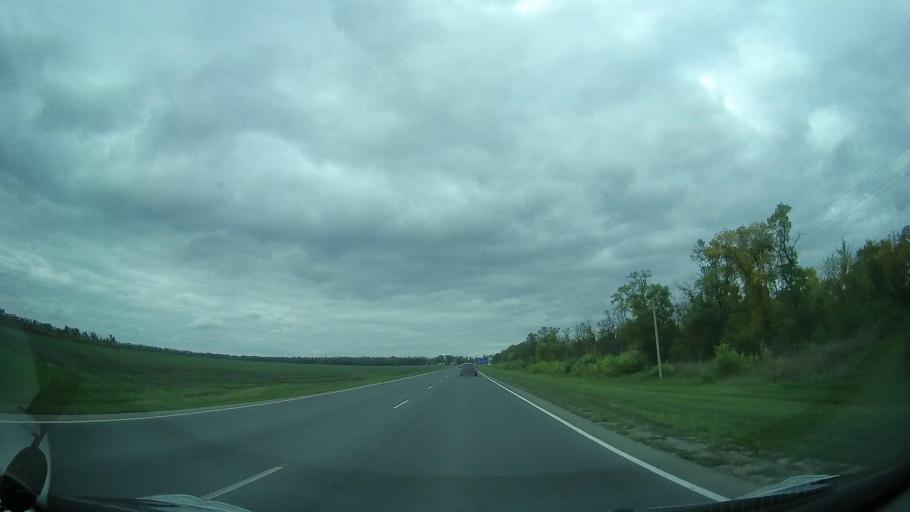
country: RU
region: Rostov
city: Yegorlykskaya
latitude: 46.5798
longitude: 40.6322
